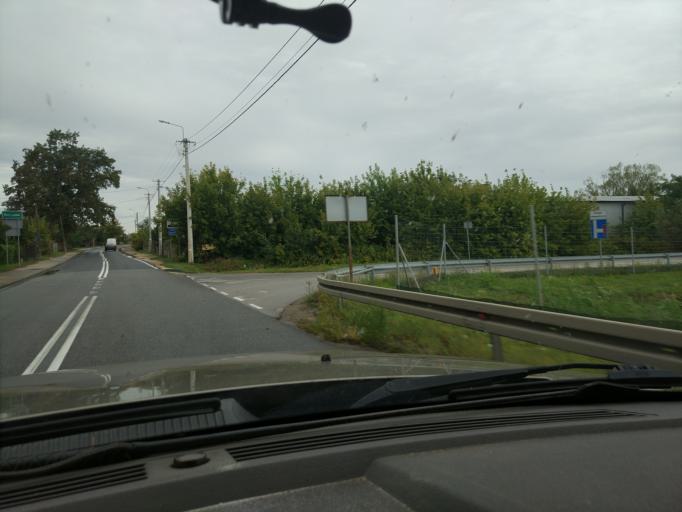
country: PL
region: Masovian Voivodeship
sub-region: Powiat warszawski zachodni
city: Ozarow Mazowiecki
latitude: 52.1856
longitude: 20.7705
